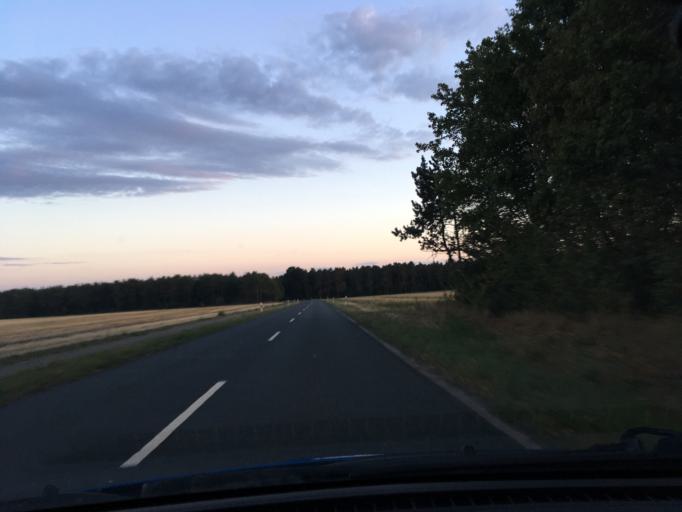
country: DE
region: Lower Saxony
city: Fassberg
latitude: 52.9236
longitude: 10.1516
